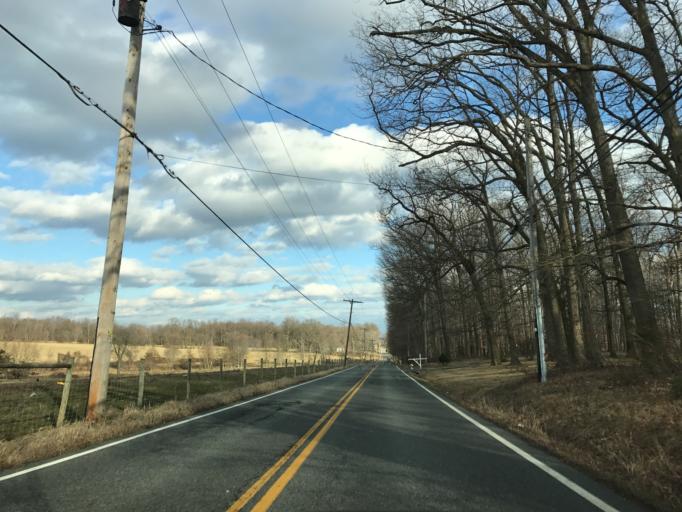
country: US
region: Maryland
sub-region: Cecil County
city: Charlestown
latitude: 39.6397
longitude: -76.0036
